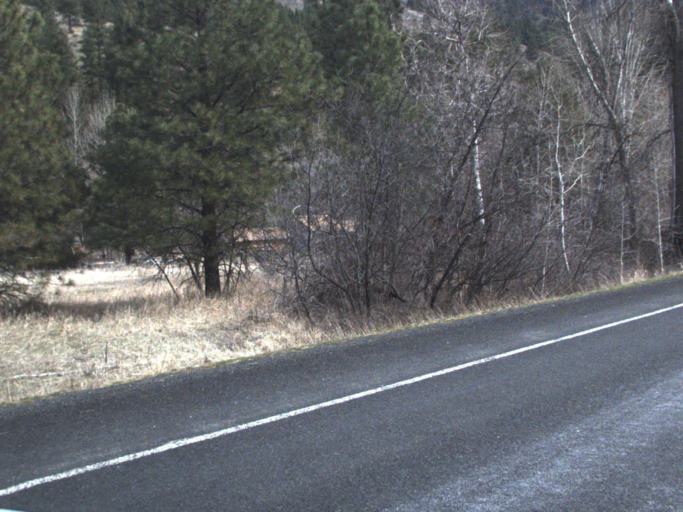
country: US
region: Washington
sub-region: Kittitas County
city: Cle Elum
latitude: 46.9018
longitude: -121.0147
